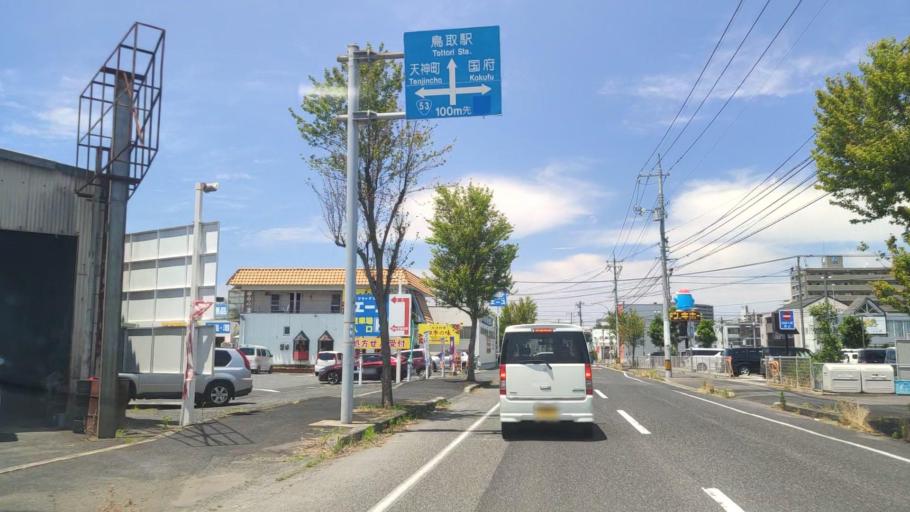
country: JP
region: Tottori
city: Tottori
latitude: 35.4875
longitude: 134.2327
